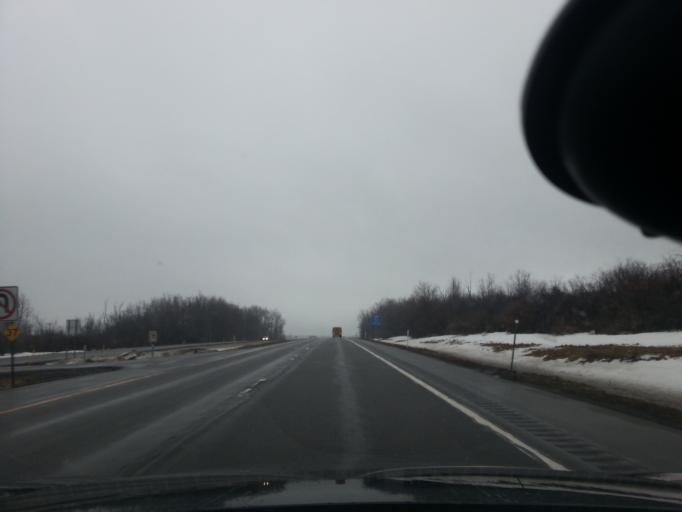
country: US
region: New York
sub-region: Jefferson County
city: Watertown
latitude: 43.9487
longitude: -75.9568
